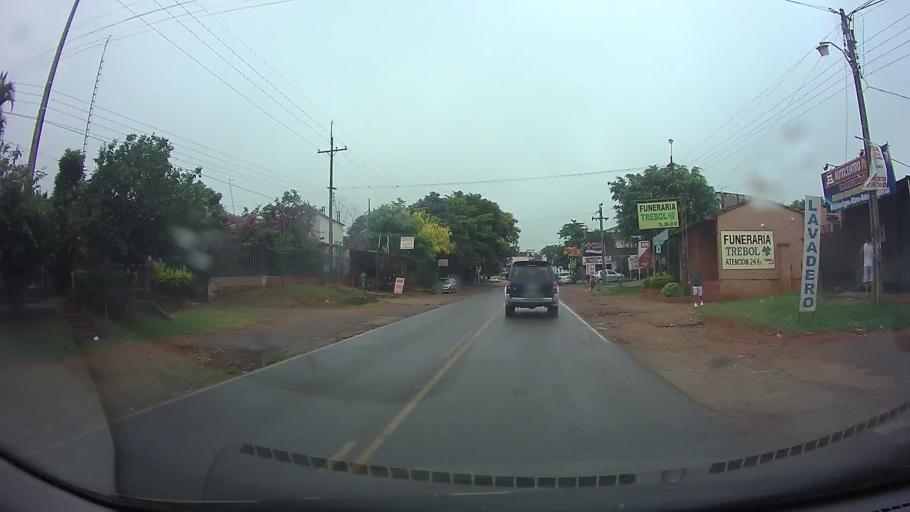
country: PY
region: Central
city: Ita
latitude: -25.4478
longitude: -57.3689
